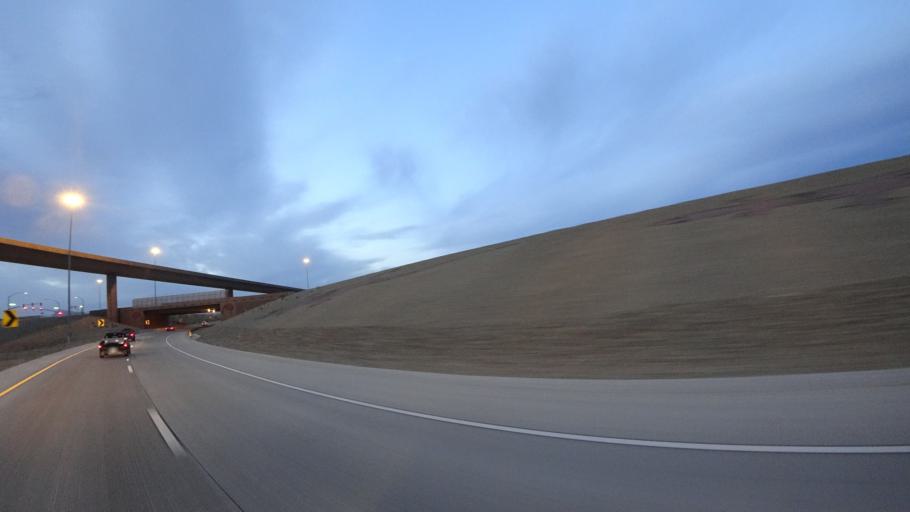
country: US
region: Arizona
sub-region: Maricopa County
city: Goodyear
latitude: 33.4634
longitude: -112.4246
